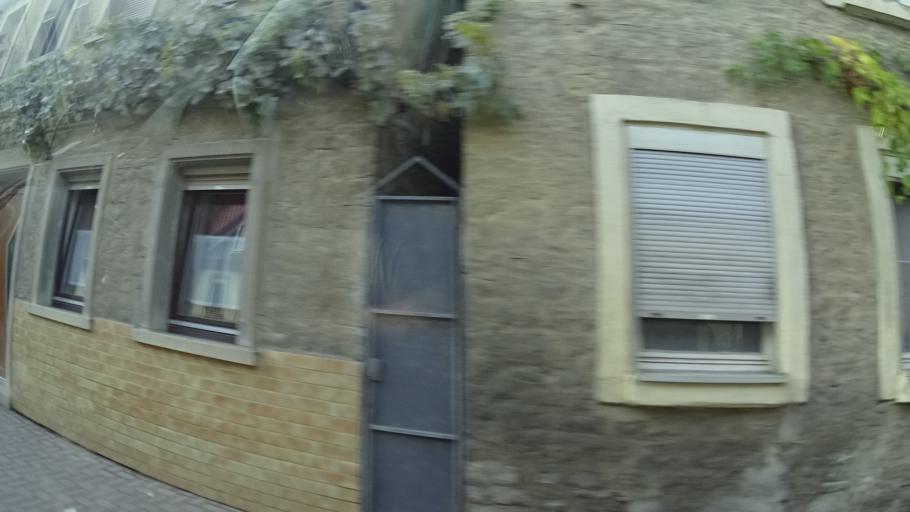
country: DE
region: Bavaria
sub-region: Regierungsbezirk Unterfranken
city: Mainstockheim
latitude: 49.7711
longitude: 10.1522
